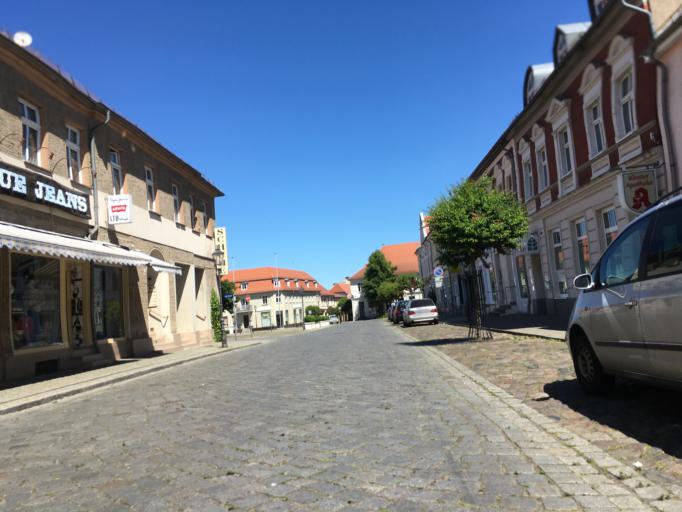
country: DE
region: Brandenburg
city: Zehdenick
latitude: 52.9786
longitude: 13.3318
